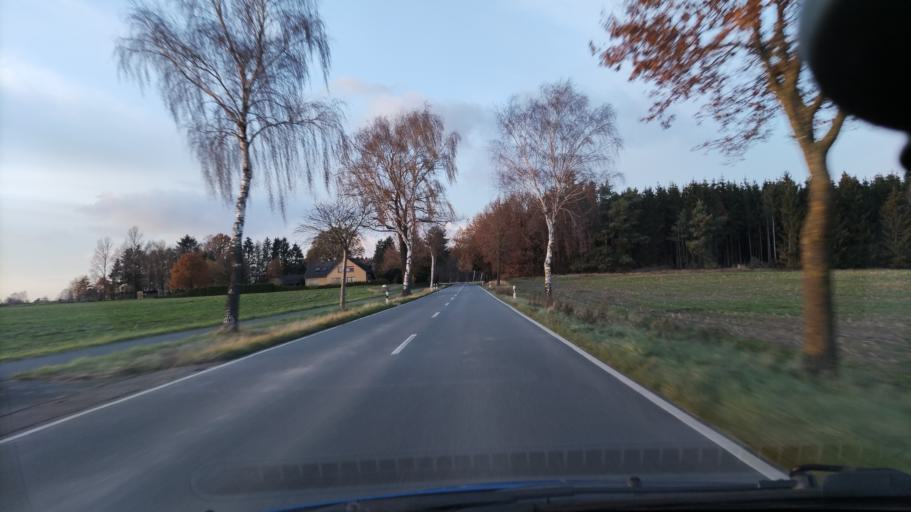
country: DE
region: Lower Saxony
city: Schneverdingen
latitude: 53.0864
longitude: 9.8502
